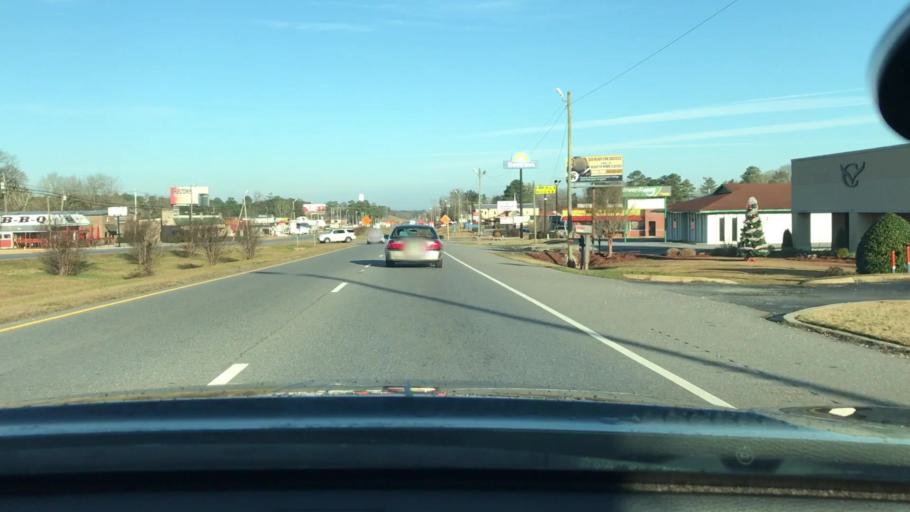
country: US
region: Alabama
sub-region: Talladega County
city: Childersburg
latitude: 33.2648
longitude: -86.3507
